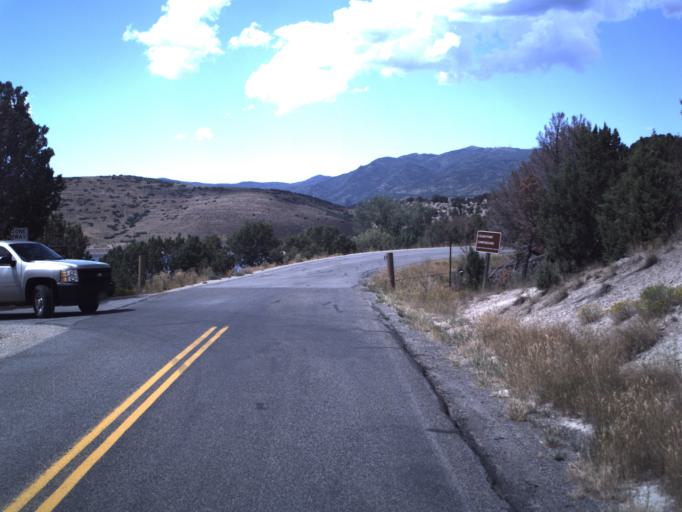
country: US
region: Utah
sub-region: Summit County
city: Oakley
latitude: 40.7835
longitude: -111.3938
